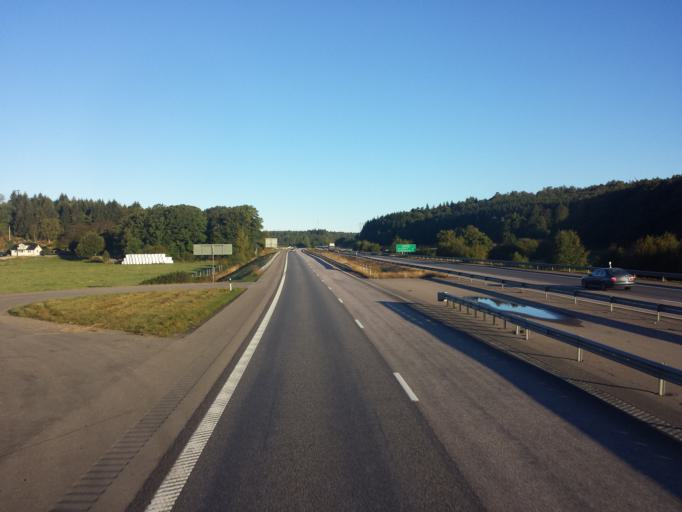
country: SE
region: Halland
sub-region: Varbergs Kommun
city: Varberg
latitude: 57.1789
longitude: 12.2710
